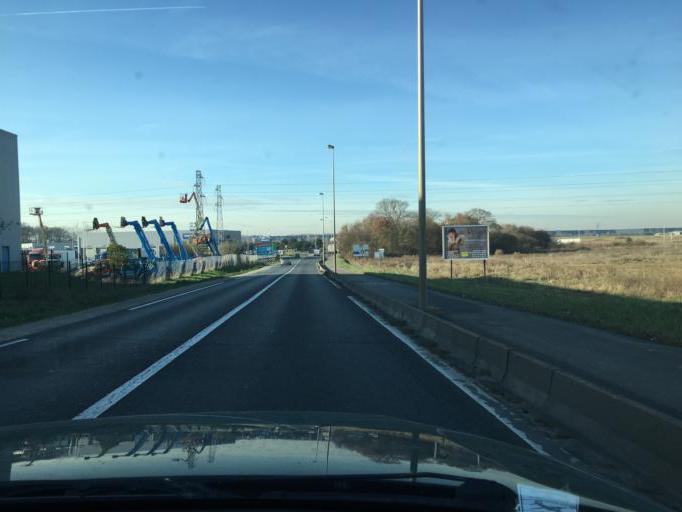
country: FR
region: Centre
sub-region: Departement du Loiret
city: Saran
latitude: 47.9513
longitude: 1.8618
